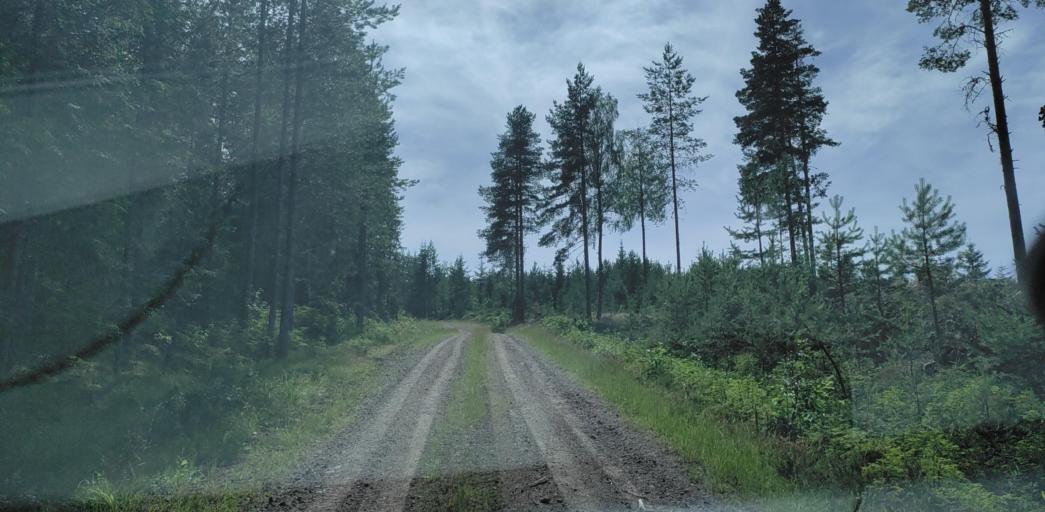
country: SE
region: Vaermland
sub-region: Hagfors Kommun
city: Ekshaerad
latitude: 60.0991
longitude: 13.3727
